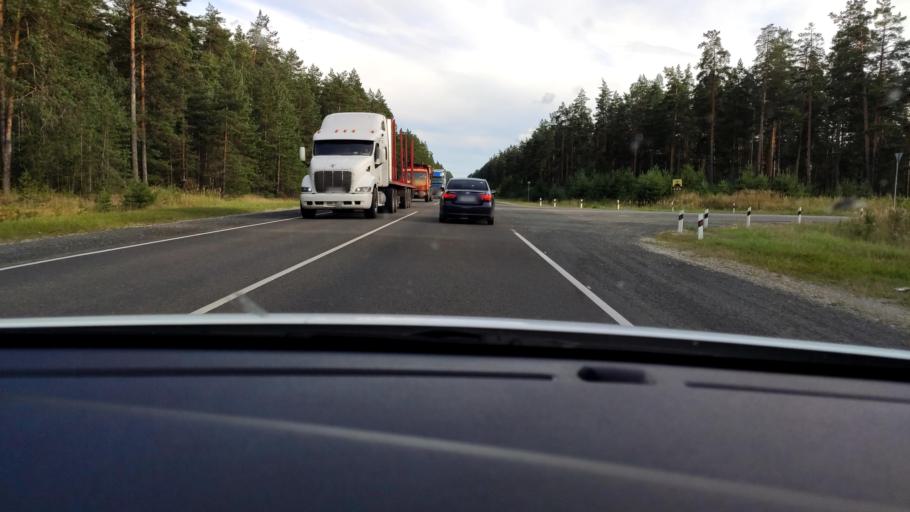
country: RU
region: Mariy-El
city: Suslonger
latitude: 56.3529
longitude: 48.2224
